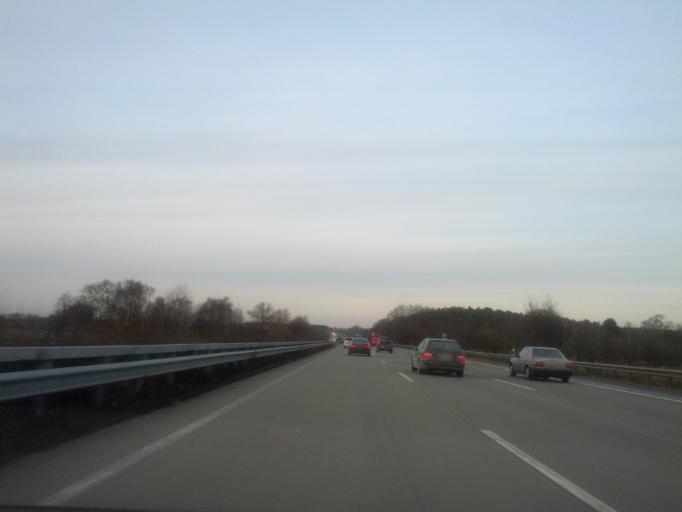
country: DE
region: Lower Saxony
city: Toppenstedt
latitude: 53.2883
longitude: 10.0782
